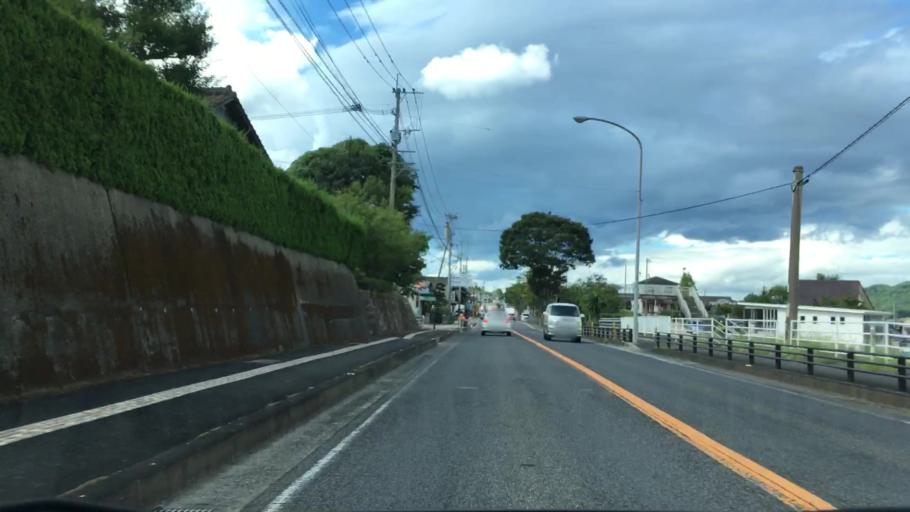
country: JP
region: Saga Prefecture
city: Imaricho-ko
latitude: 33.2081
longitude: 129.8502
